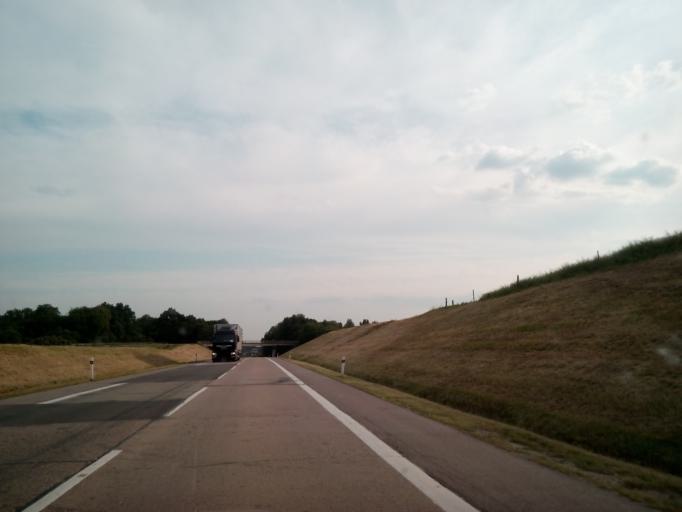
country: SK
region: Trenciansky
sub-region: Okres Trencin
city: Trencin
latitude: 48.8765
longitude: 17.9600
